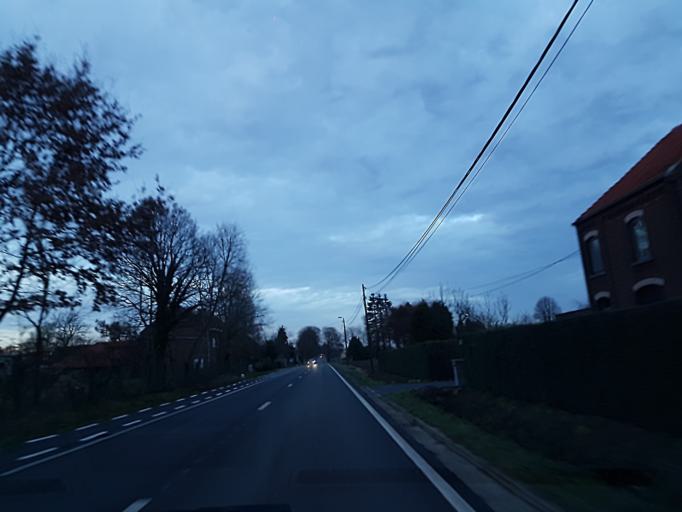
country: BE
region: Flanders
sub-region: Provincie Vlaams-Brabant
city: Lubbeek
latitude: 50.8866
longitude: 4.8794
